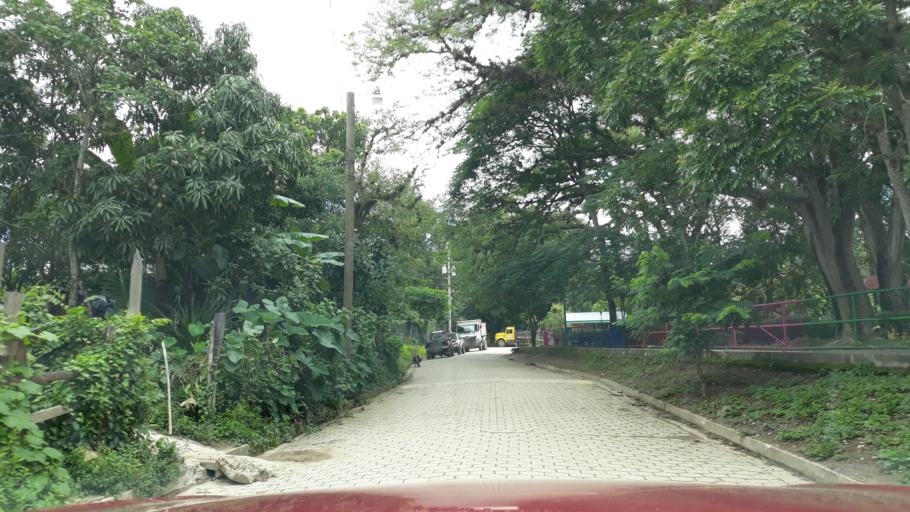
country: HN
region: El Paraiso
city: Santa Cruz
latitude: 13.7317
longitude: -86.6228
